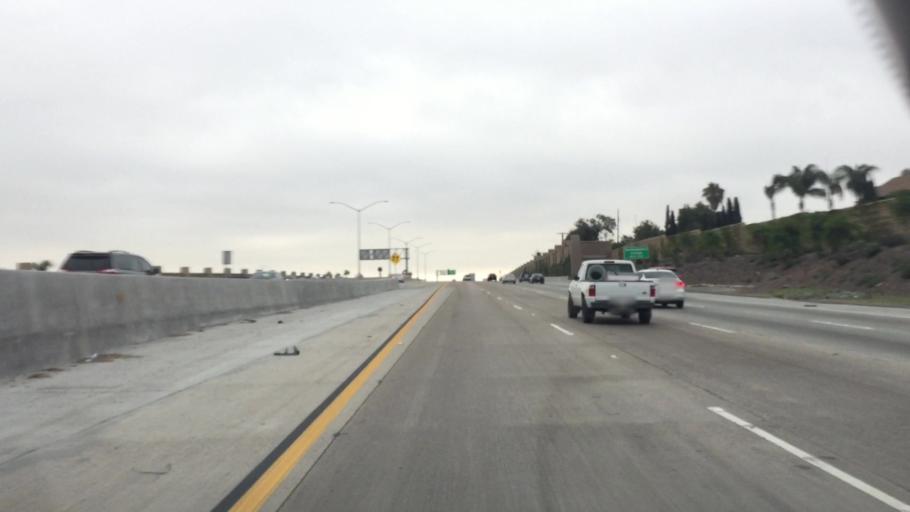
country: US
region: California
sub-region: San Diego County
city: Bonita
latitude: 32.6170
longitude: -117.0387
